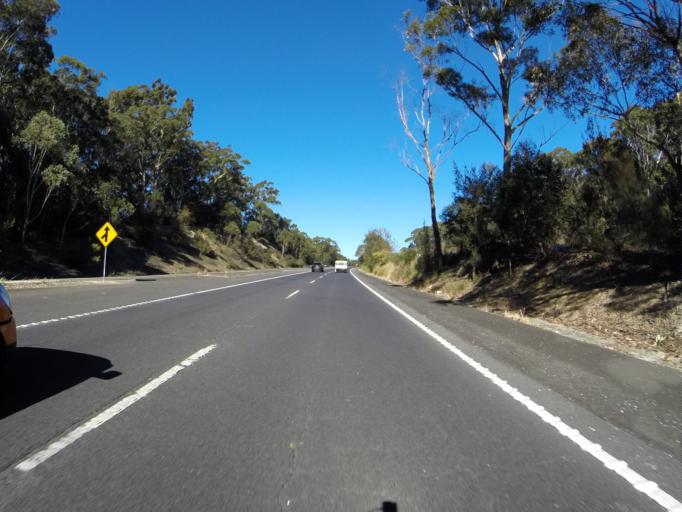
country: AU
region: New South Wales
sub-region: Wollongong
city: Helensburgh
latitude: -34.2038
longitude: 150.9649
